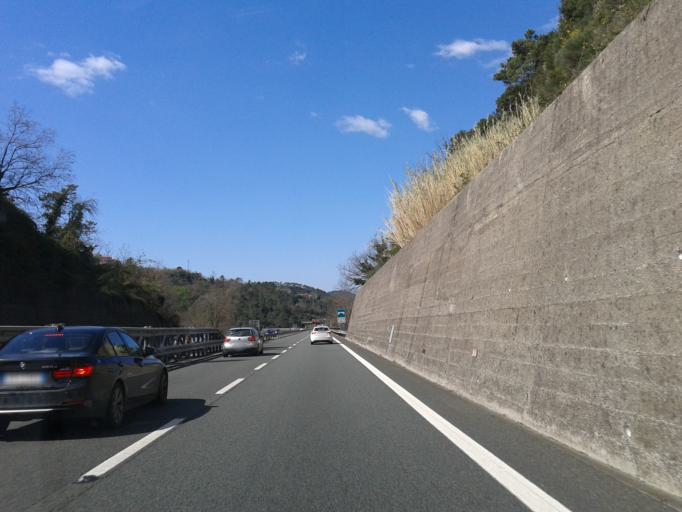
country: IT
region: Liguria
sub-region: Provincia di Genova
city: Casarza Ligure
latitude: 44.2707
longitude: 9.4640
